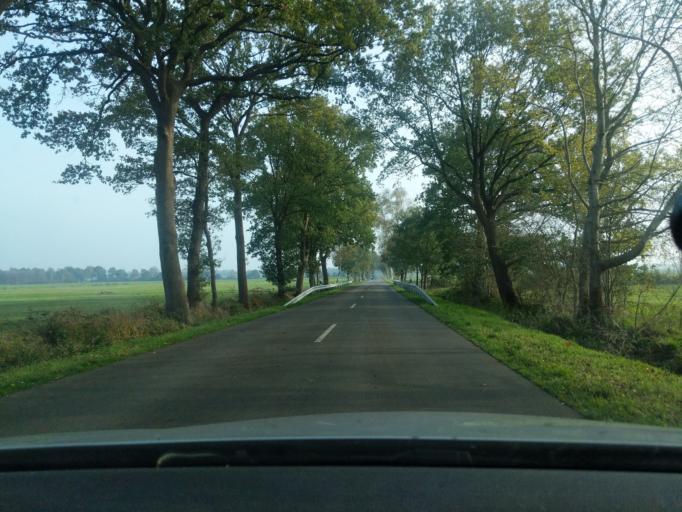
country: DE
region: Lower Saxony
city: Stinstedt
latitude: 53.6561
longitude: 8.9808
